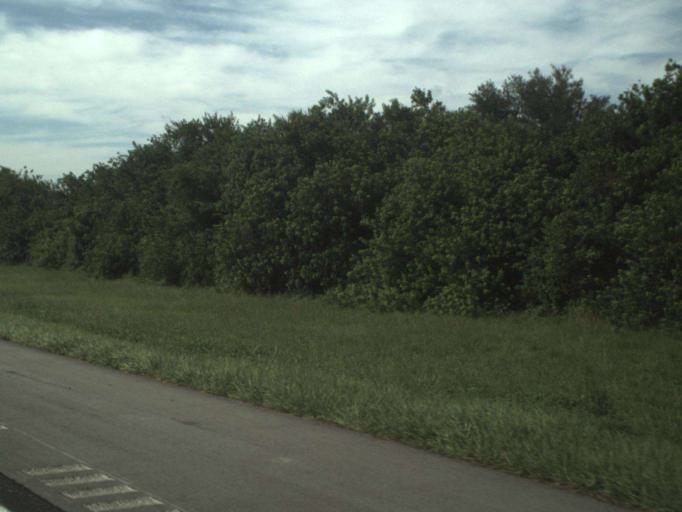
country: US
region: Florida
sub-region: Indian River County
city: West Vero Corridor
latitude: 27.5982
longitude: -80.5058
